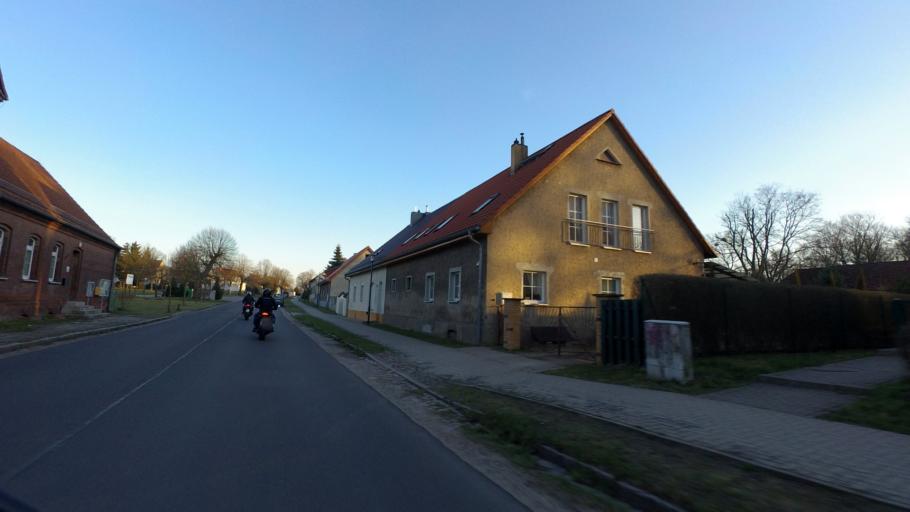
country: DE
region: Berlin
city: Hellersdorf
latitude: 52.5464
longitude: 13.6377
